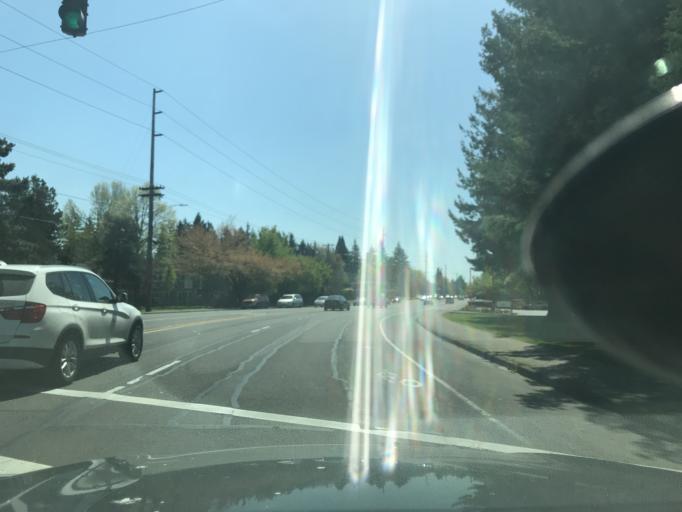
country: US
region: Oregon
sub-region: Multnomah County
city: Fairview
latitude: 45.5157
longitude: -122.4762
